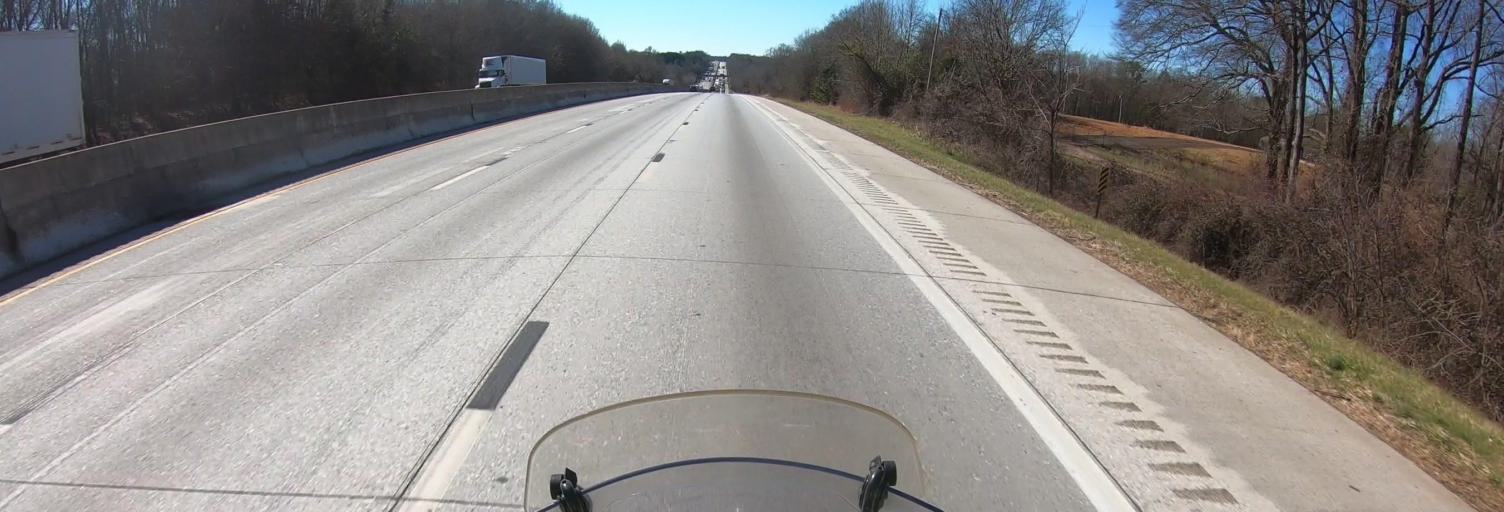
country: US
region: South Carolina
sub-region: Anderson County
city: Williamston
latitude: 34.6557
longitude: -82.5649
